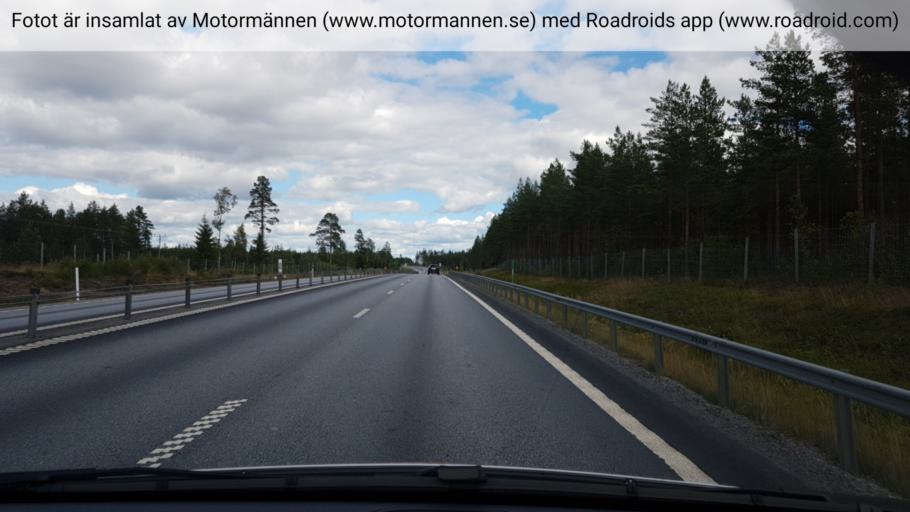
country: SE
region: Vaesterbotten
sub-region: Umea Kommun
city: Hoernefors
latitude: 63.6457
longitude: 19.9362
